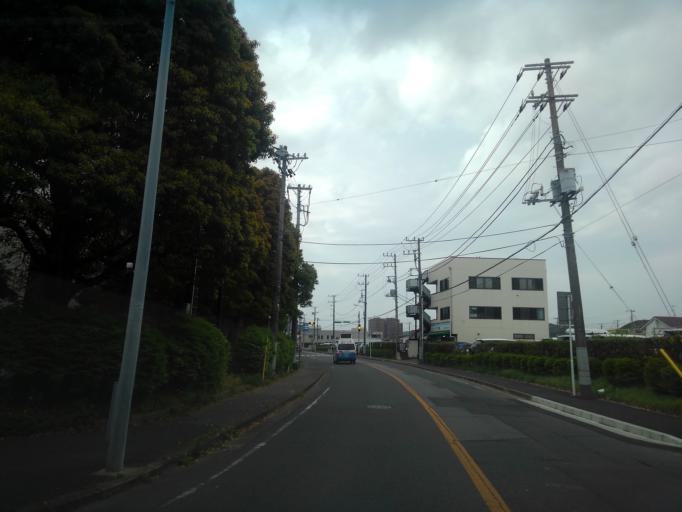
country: JP
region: Chiba
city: Kimitsu
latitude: 35.3307
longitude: 139.9032
